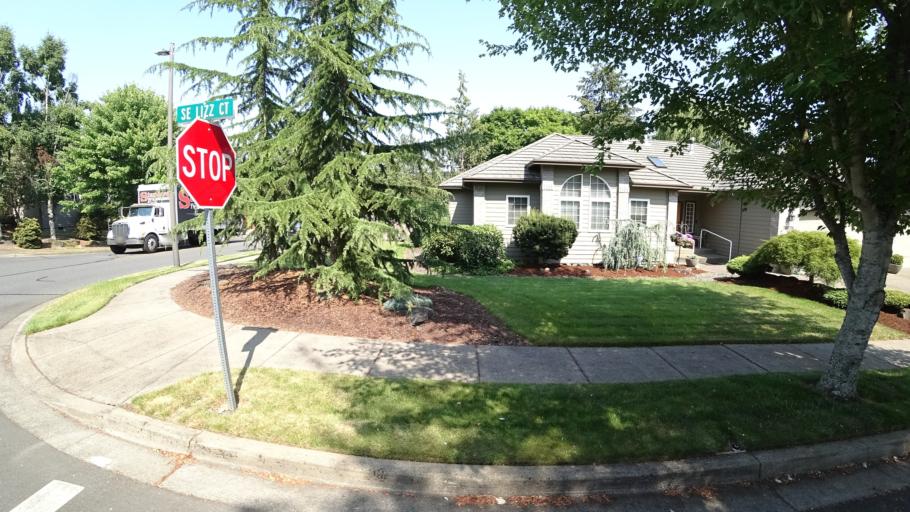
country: US
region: Oregon
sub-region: Clackamas County
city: Happy Valley
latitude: 45.4446
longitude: -122.5322
